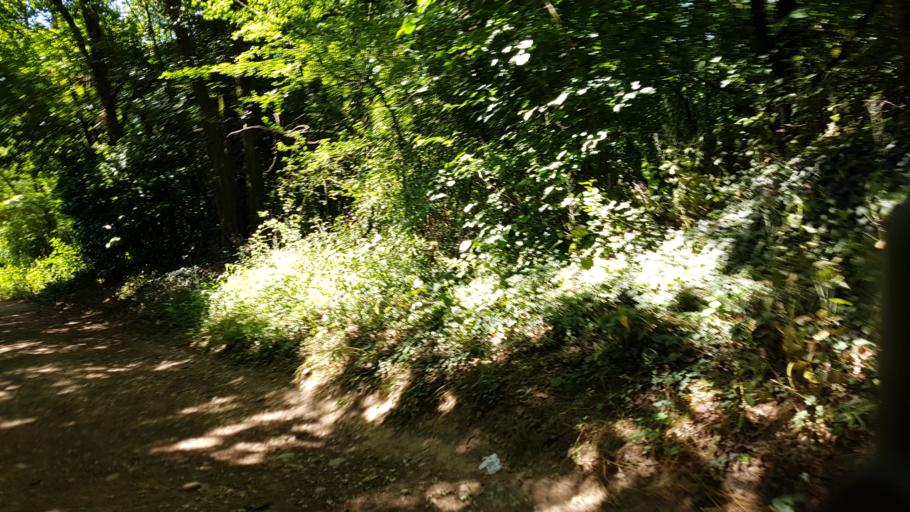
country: FR
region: Rhone-Alpes
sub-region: Departement du Rhone
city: Sathonay-Camp
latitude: 45.8346
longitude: 4.8665
